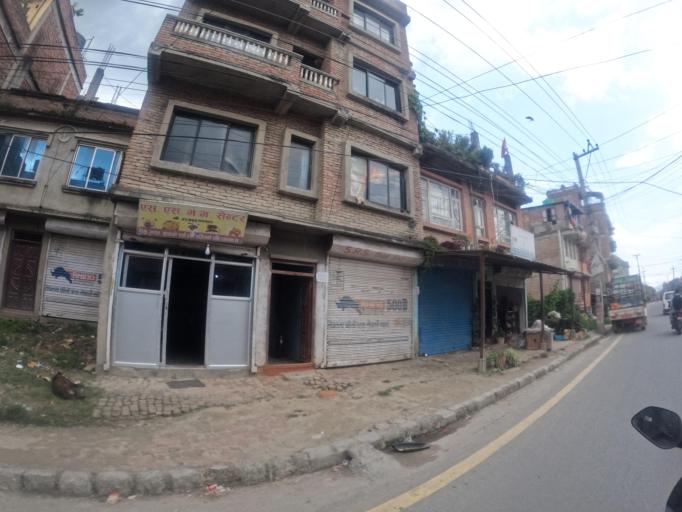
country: NP
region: Central Region
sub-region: Bagmati Zone
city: Bhaktapur
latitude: 27.6794
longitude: 85.4016
